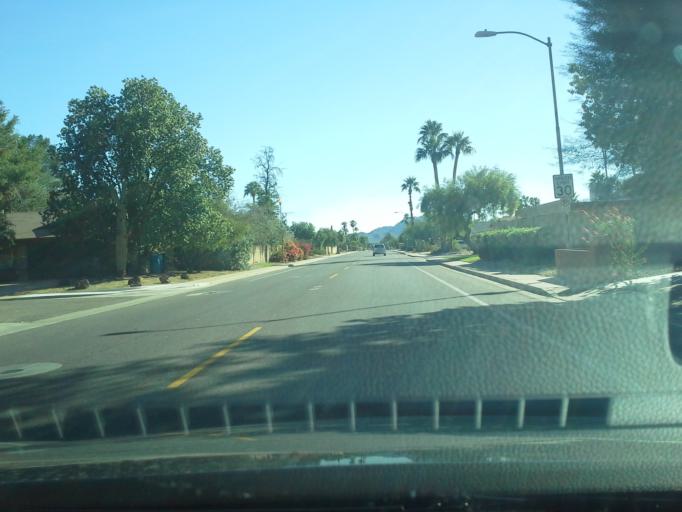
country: US
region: Arizona
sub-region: Maricopa County
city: Paradise Valley
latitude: 33.6176
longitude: -111.9866
